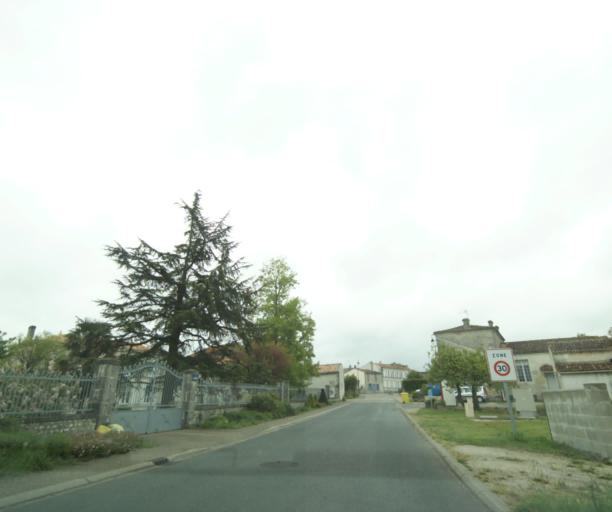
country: FR
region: Poitou-Charentes
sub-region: Departement de la Charente-Maritime
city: Pons
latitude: 45.6435
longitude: -0.5531
